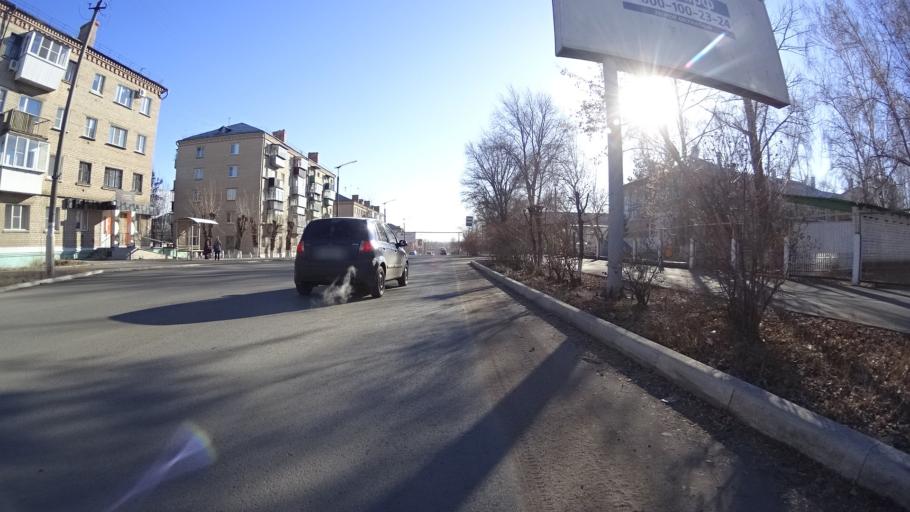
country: RU
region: Chelyabinsk
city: Troitsk
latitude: 54.0809
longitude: 61.5355
